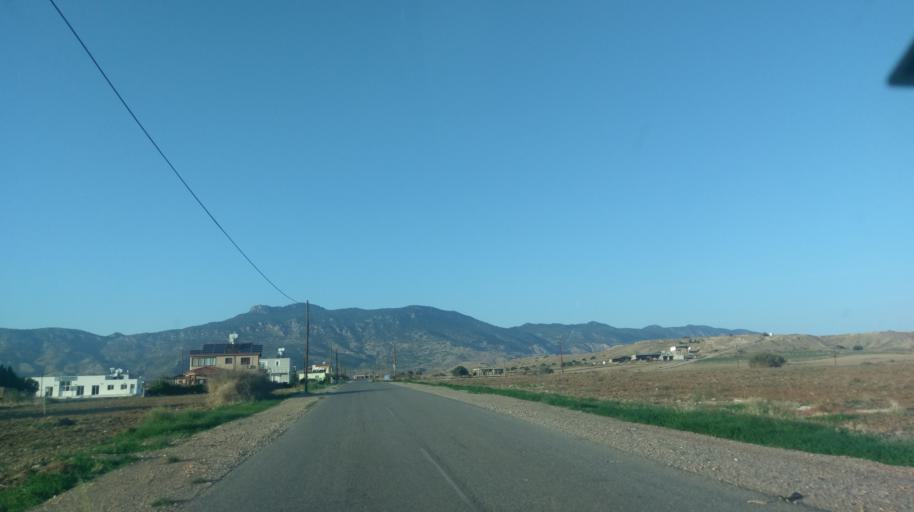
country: CY
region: Larnaka
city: Athienou
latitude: 35.2370
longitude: 33.5548
